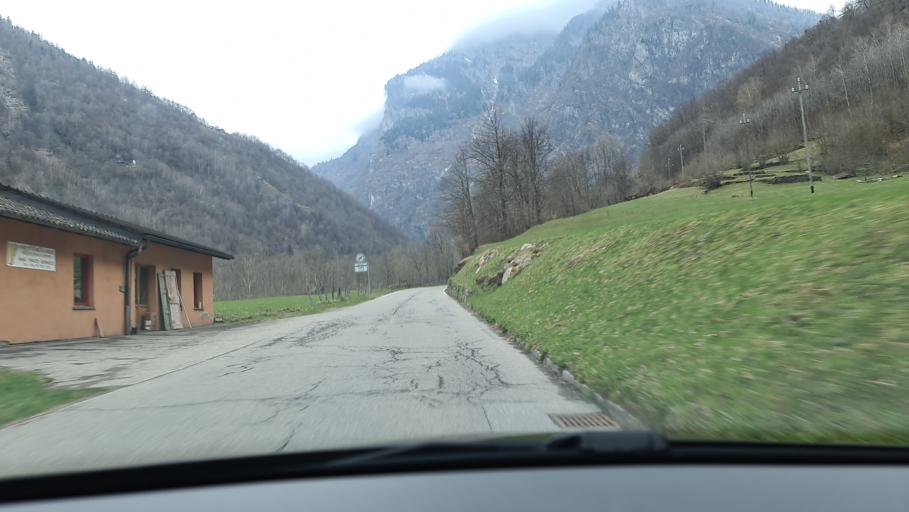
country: CH
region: Ticino
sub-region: Vallemaggia District
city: Cevio
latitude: 46.4000
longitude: 8.6524
